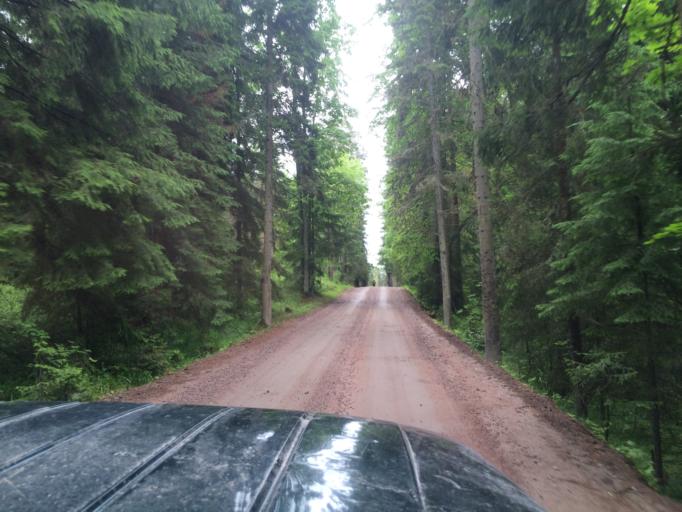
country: RU
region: Republic of Karelia
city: Sortavala
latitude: 61.3697
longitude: 30.9038
